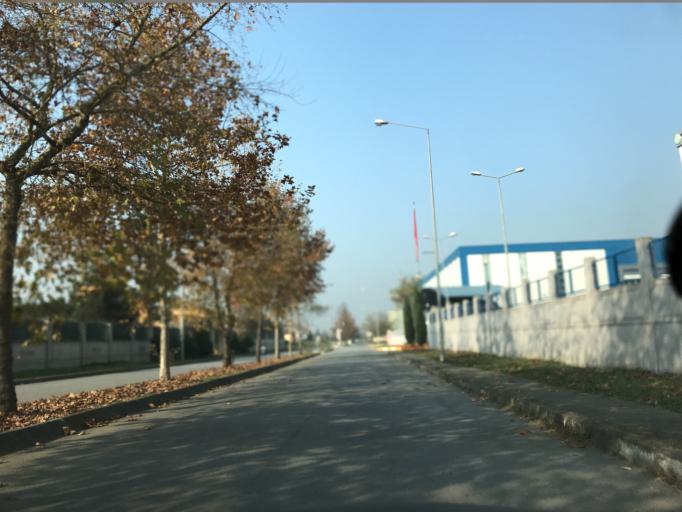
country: TR
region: Duzce
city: Duzce
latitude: 40.7881
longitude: 31.1345
